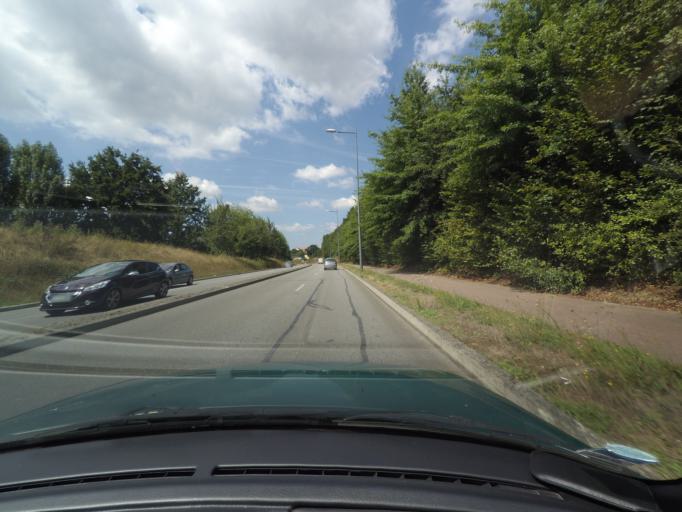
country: FR
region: Limousin
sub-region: Departement de la Haute-Vienne
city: Condat-sur-Vienne
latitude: 45.8062
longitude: 1.2703
